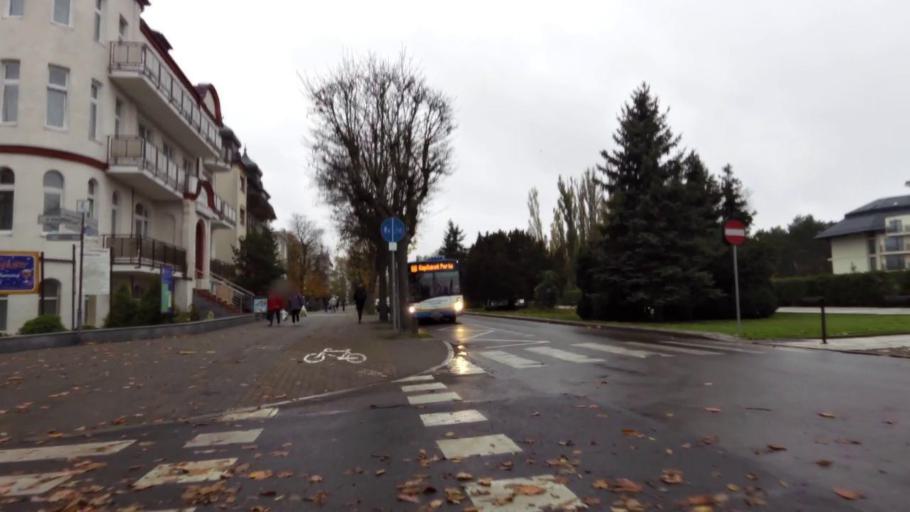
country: PL
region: West Pomeranian Voivodeship
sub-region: Swinoujscie
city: Swinoujscie
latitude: 53.9198
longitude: 14.2508
